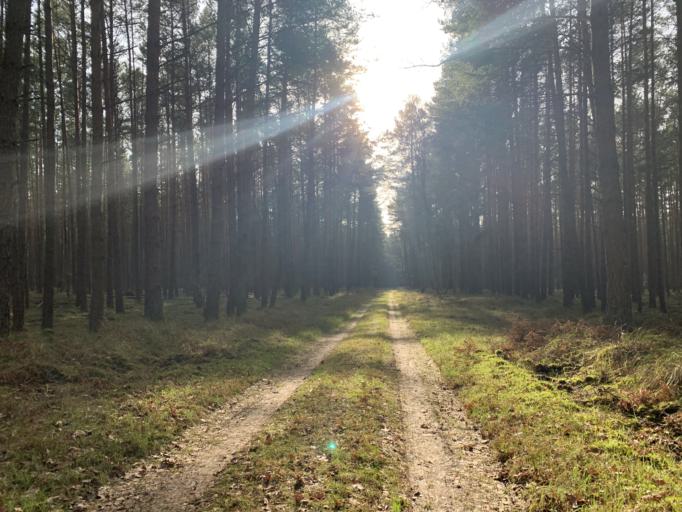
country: DE
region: Mecklenburg-Vorpommern
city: Wesenberg
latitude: 53.2854
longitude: 12.8622
